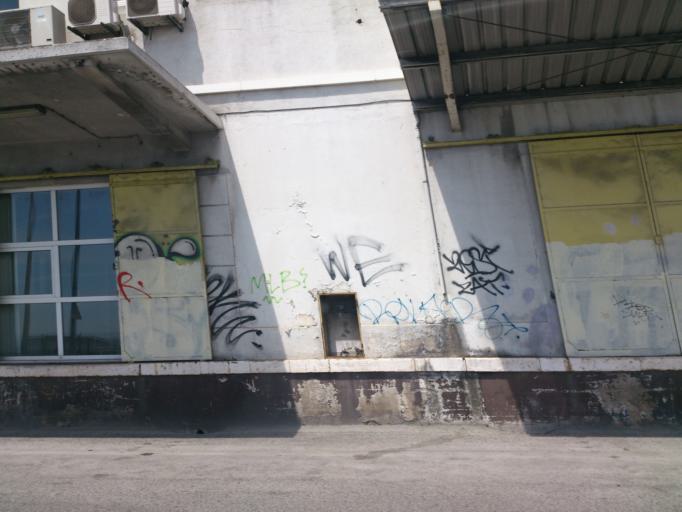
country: PT
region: Lisbon
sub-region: Lisbon
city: Lisbon
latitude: 38.7173
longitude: -9.1186
